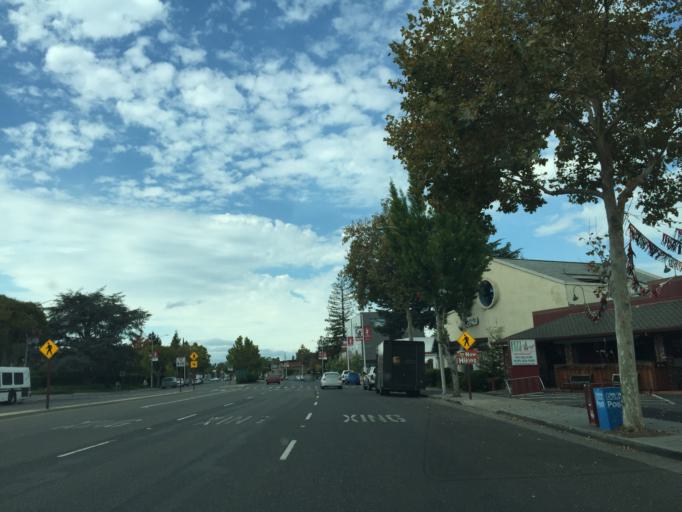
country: US
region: California
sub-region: Santa Clara County
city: Los Altos
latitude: 37.4139
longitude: -122.1260
